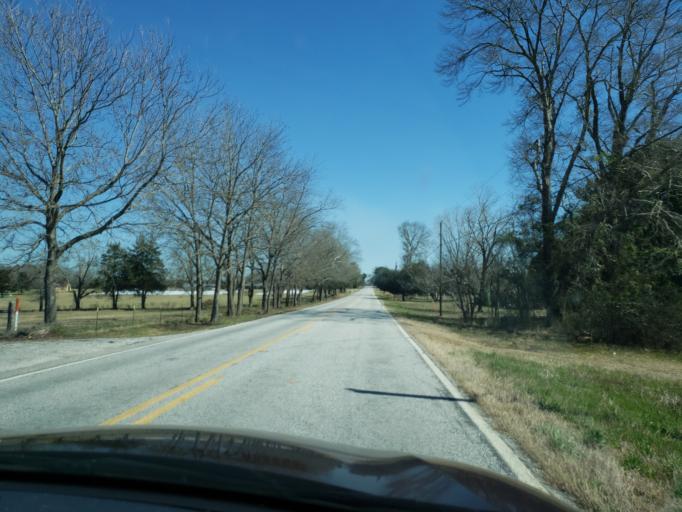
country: US
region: Alabama
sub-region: Elmore County
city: Tallassee
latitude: 32.5814
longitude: -85.7602
